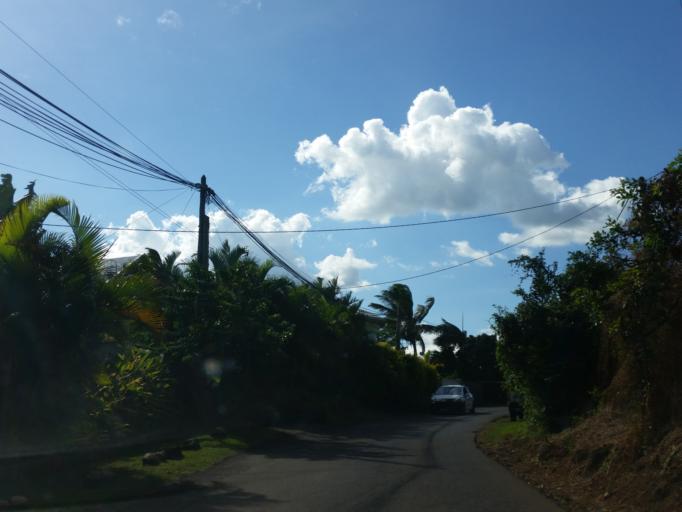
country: RE
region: Reunion
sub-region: Reunion
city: Saint-Pierre
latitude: -21.3248
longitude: 55.4992
